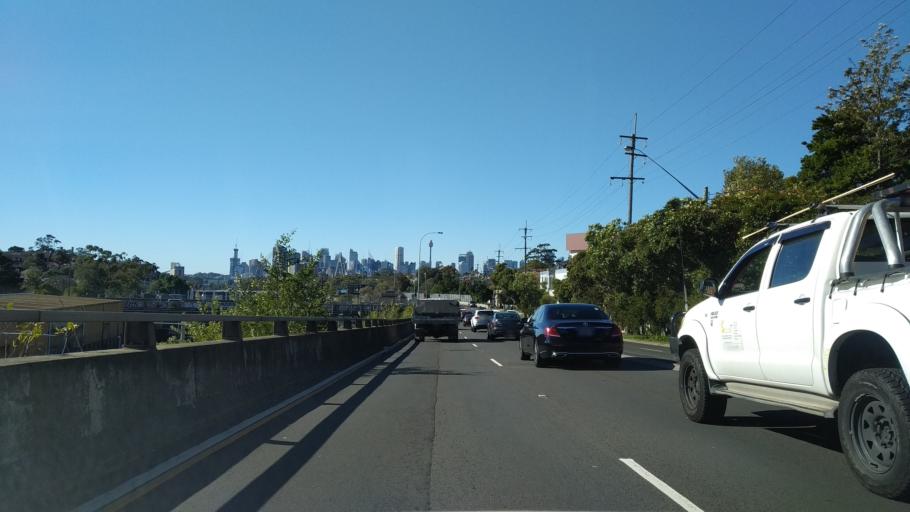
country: AU
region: New South Wales
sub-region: Leichhardt
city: Lilyfield
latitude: -33.8745
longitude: 151.1627
